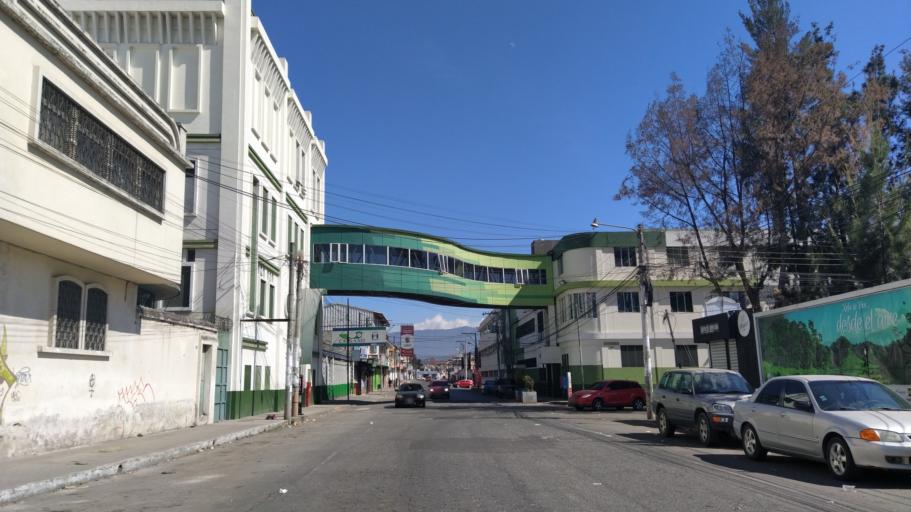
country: GT
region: Quetzaltenango
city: Quetzaltenango
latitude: 14.8431
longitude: -91.5188
